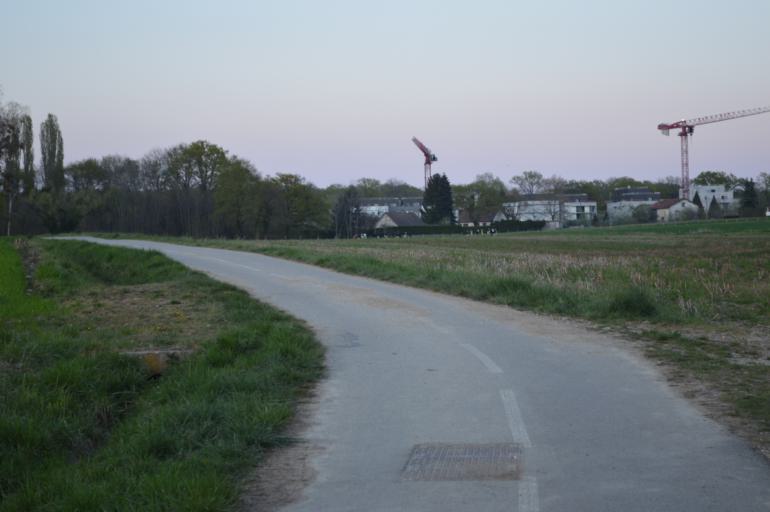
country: FR
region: Rhone-Alpes
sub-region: Departement de l'Ain
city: Ornex
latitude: 46.2724
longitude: 6.0867
